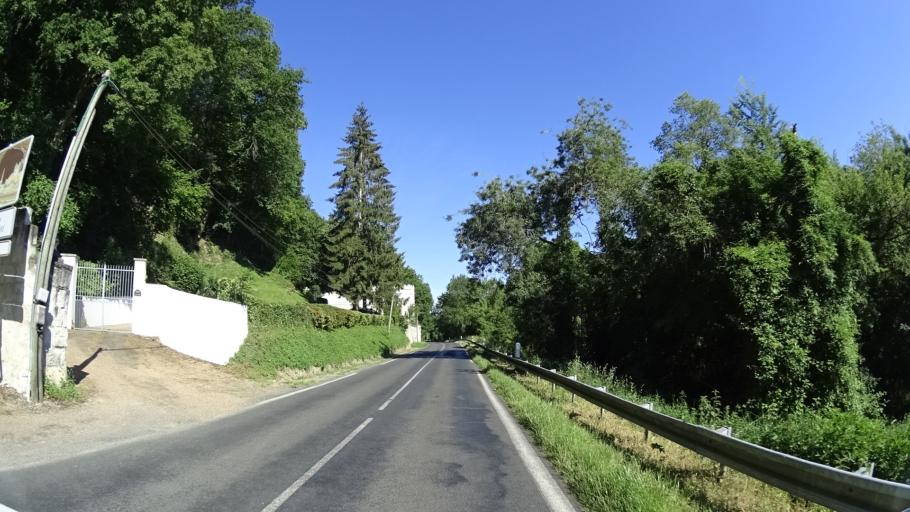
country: FR
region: Pays de la Loire
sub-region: Departement de Maine-et-Loire
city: Saint-Martin-de-la-Place
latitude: 47.2832
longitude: -0.1233
